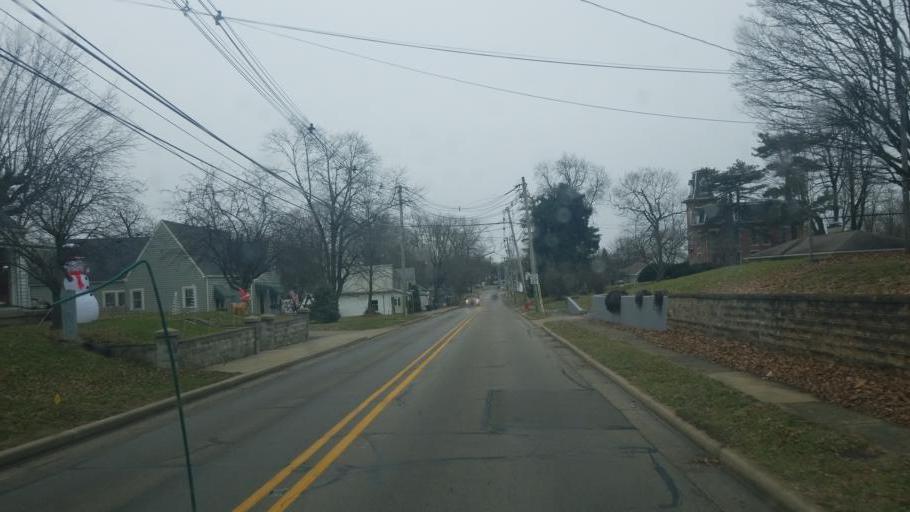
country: US
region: Indiana
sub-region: Henry County
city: Knightstown
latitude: 39.7977
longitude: -85.5322
